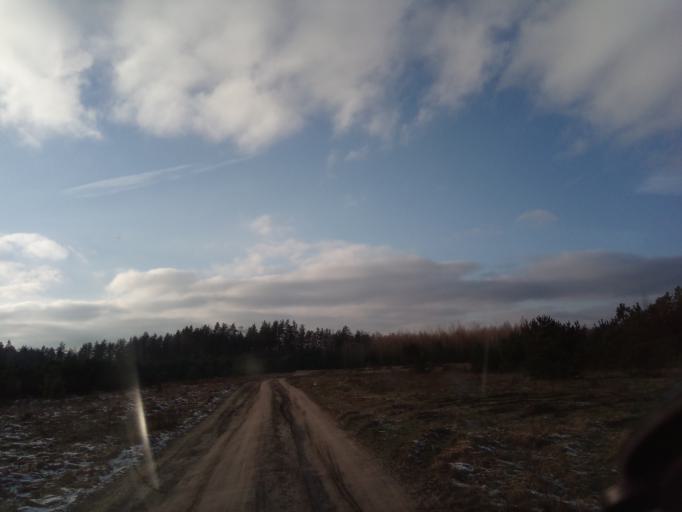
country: LT
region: Alytaus apskritis
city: Druskininkai
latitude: 53.9412
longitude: 24.2750
